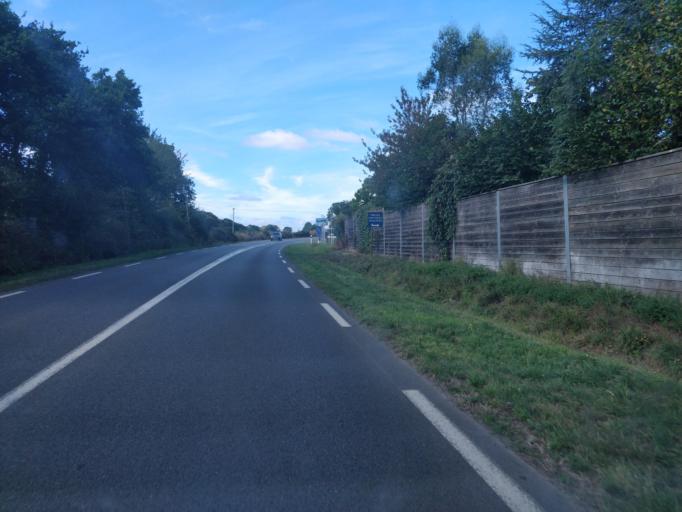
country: FR
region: Brittany
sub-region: Departement des Cotes-d'Armor
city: Erquy
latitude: 48.5939
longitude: -2.4836
